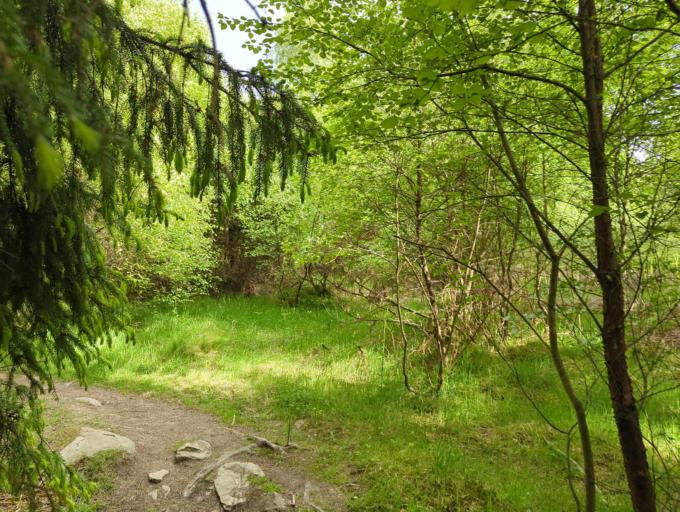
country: GB
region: Scotland
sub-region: Perth and Kinross
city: Bankfoot
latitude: 56.5528
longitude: -3.6132
